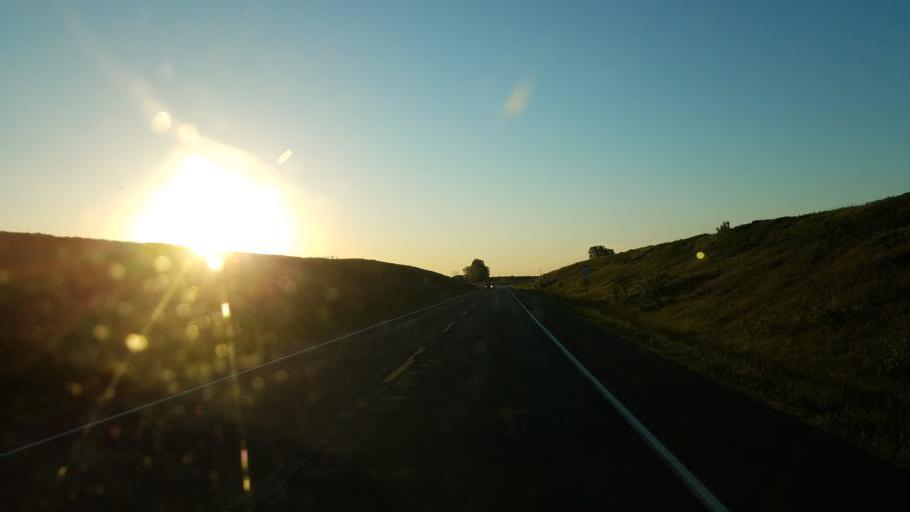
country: US
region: Missouri
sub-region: Schuyler County
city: Lancaster
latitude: 40.4928
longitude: -92.5607
